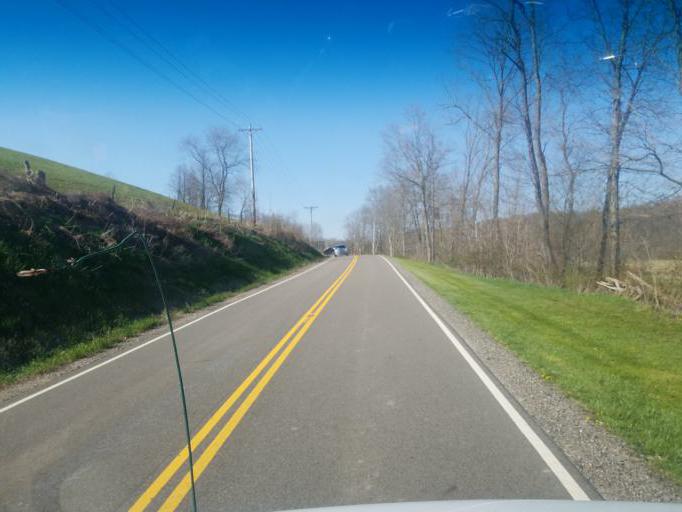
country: US
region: Ohio
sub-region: Muskingum County
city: Frazeysburg
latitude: 40.2953
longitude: -82.0872
